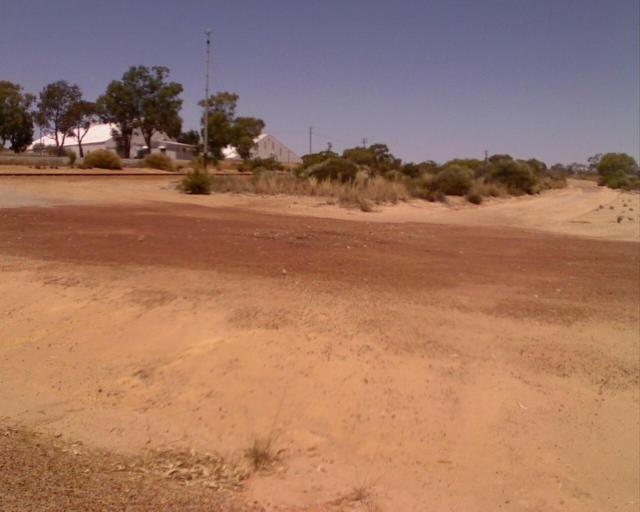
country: AU
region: Western Australia
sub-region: Merredin
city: Merredin
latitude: -30.8146
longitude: 117.8632
